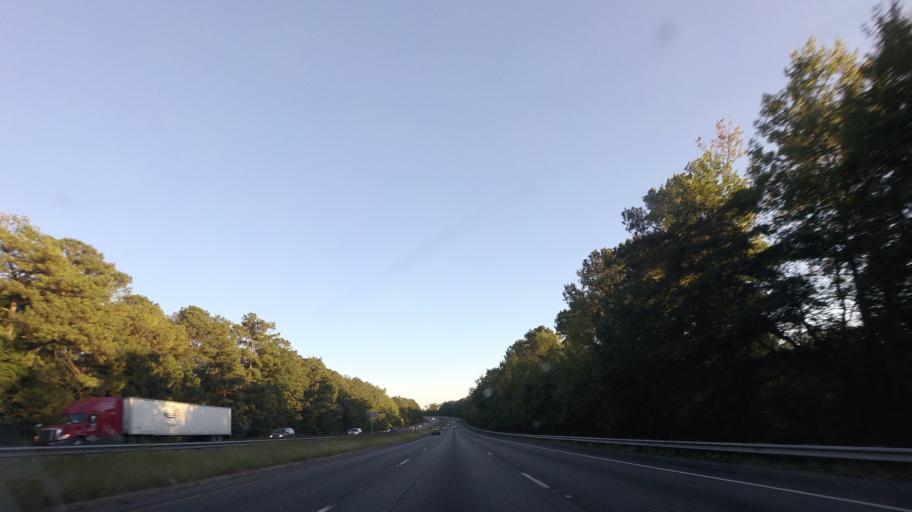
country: US
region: Georgia
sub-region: Butts County
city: Indian Springs
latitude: 33.1521
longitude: -84.0333
